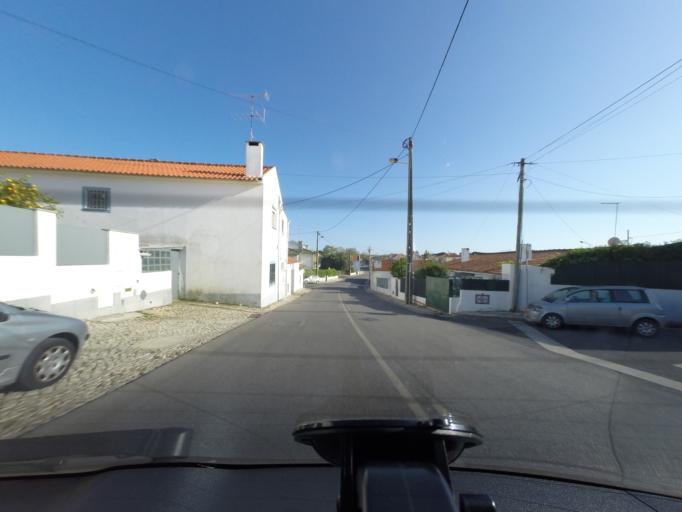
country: PT
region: Lisbon
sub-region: Cascais
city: Alcabideche
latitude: 38.7341
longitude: -9.4395
